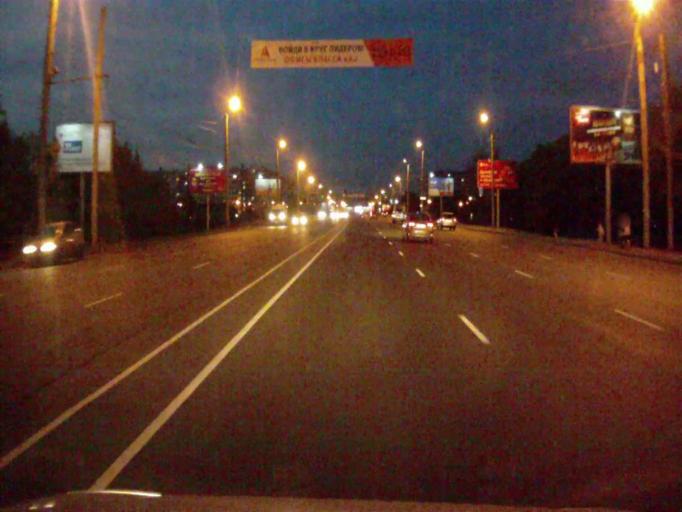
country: RU
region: Chelyabinsk
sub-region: Gorod Chelyabinsk
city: Chelyabinsk
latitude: 55.1725
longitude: 61.3582
